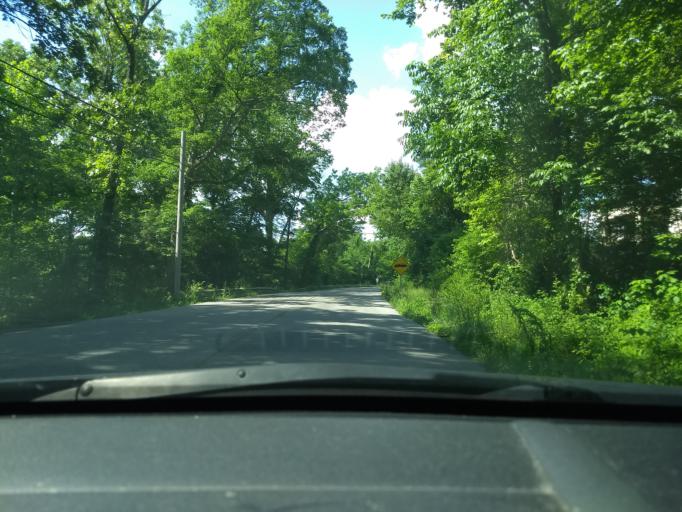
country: US
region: Indiana
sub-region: Floyd County
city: New Albany
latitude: 38.2613
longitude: -85.8619
